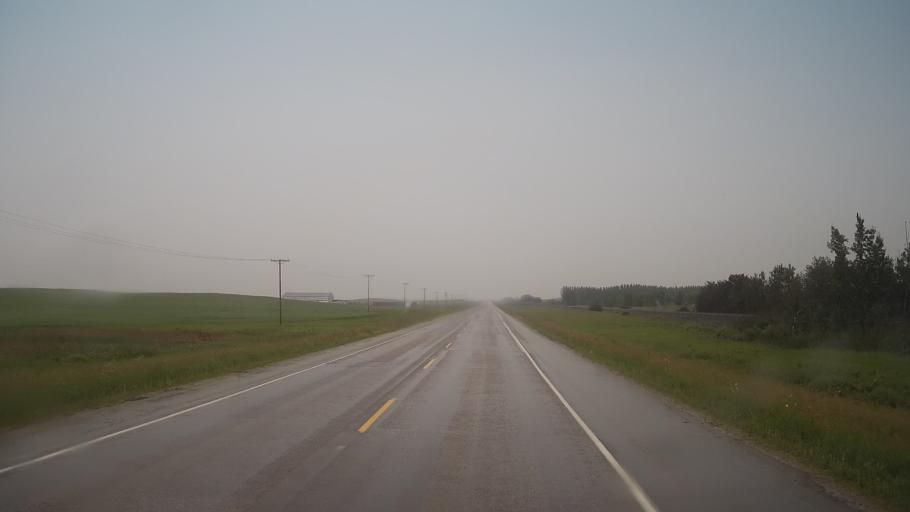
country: CA
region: Saskatchewan
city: Biggar
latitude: 52.0862
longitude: -108.0428
